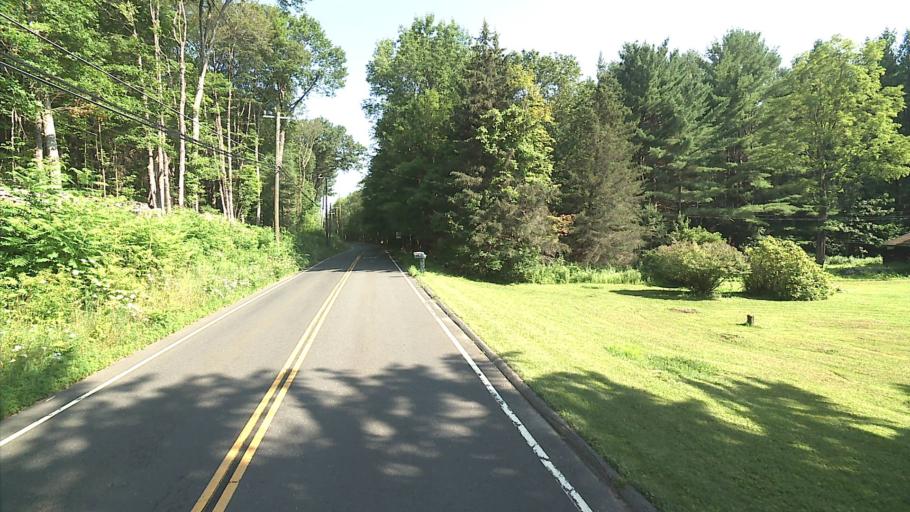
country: US
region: Connecticut
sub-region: Litchfield County
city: Winsted
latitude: 41.9953
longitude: -73.0997
